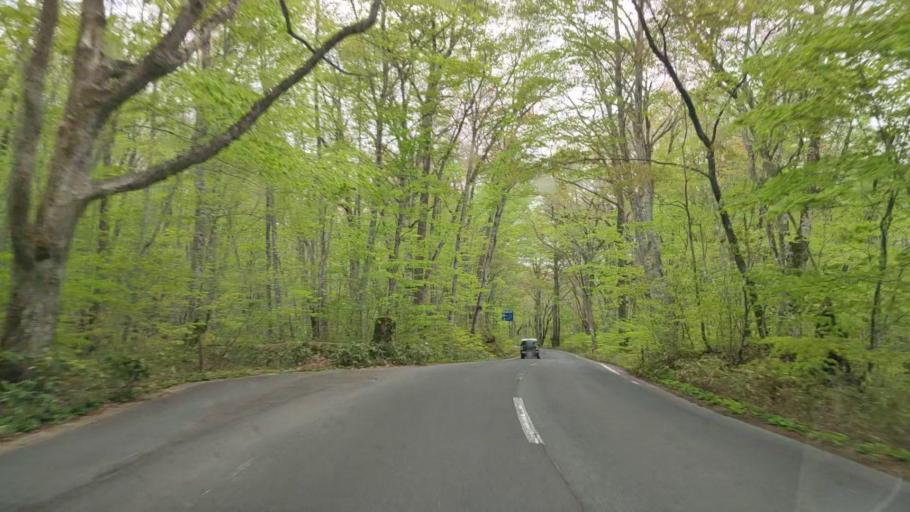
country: JP
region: Aomori
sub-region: Aomori Shi
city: Furudate
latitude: 40.5549
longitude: 140.9716
